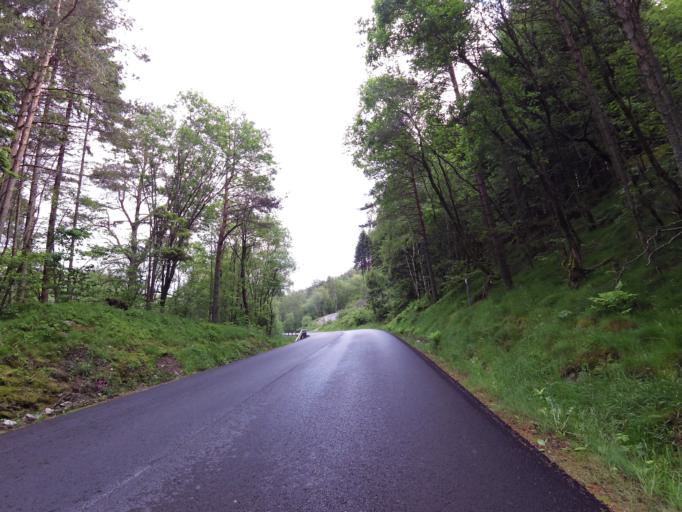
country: NO
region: Vest-Agder
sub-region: Lindesnes
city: Vigeland
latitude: 58.0551
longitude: 7.2152
